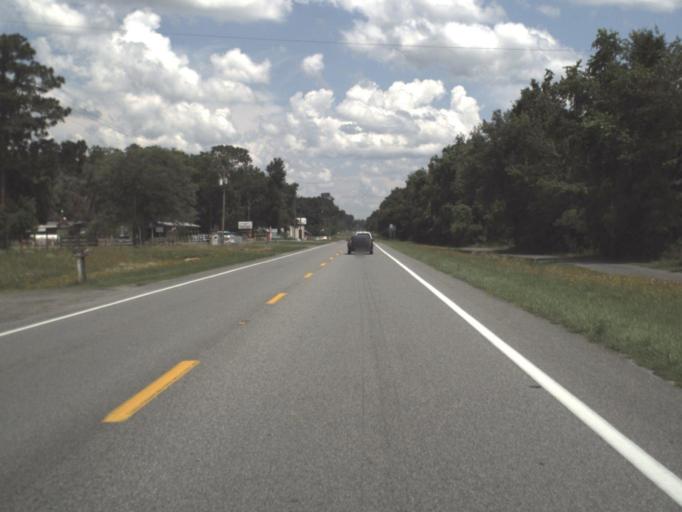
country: US
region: Florida
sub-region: Alachua County
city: High Springs
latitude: 29.9339
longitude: -82.7306
